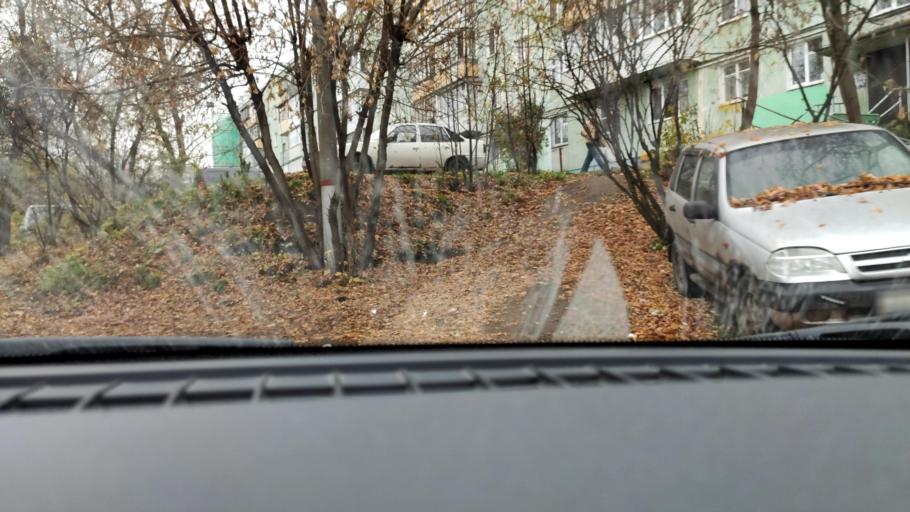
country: RU
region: Perm
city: Perm
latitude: 57.9938
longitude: 56.2015
